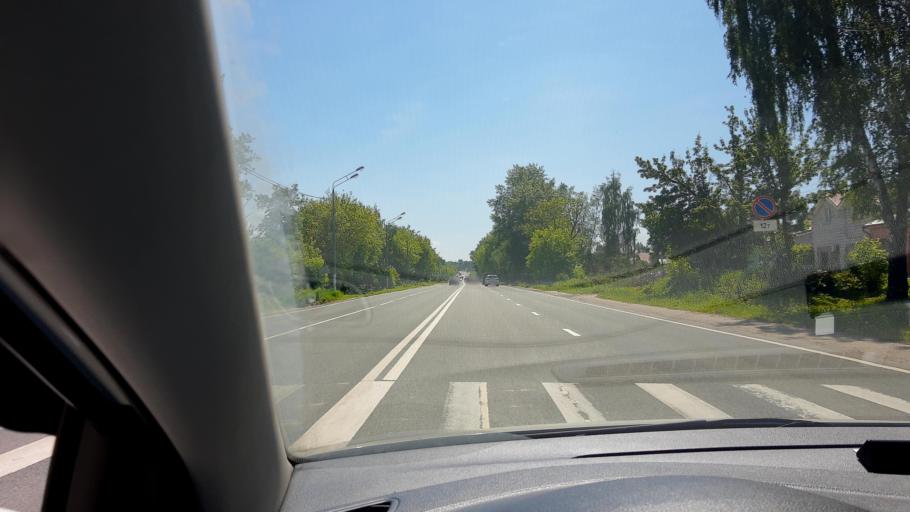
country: RU
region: Moskovskaya
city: Bronnitsy
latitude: 55.4669
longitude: 38.1993
